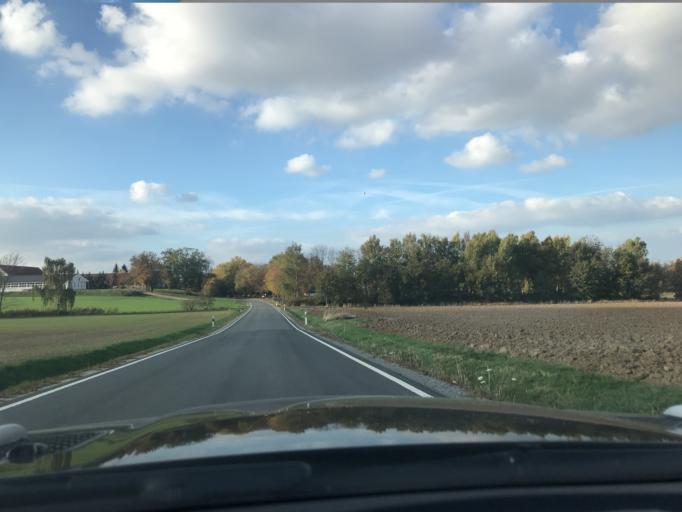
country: DE
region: Thuringia
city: Flarchheim
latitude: 51.1225
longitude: 10.4849
